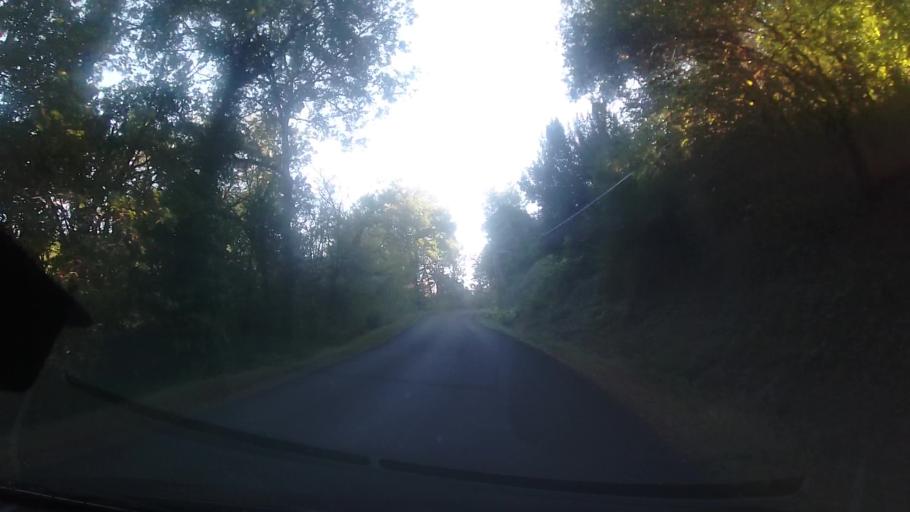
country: FR
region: Aquitaine
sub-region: Departement de la Dordogne
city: Cenac-et-Saint-Julien
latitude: 44.7900
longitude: 1.1865
